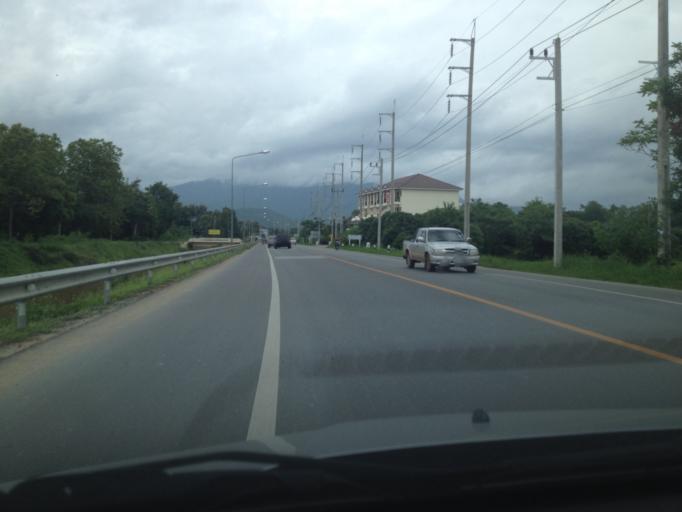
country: TH
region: Chiang Mai
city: Hang Dong
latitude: 18.7201
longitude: 98.9285
